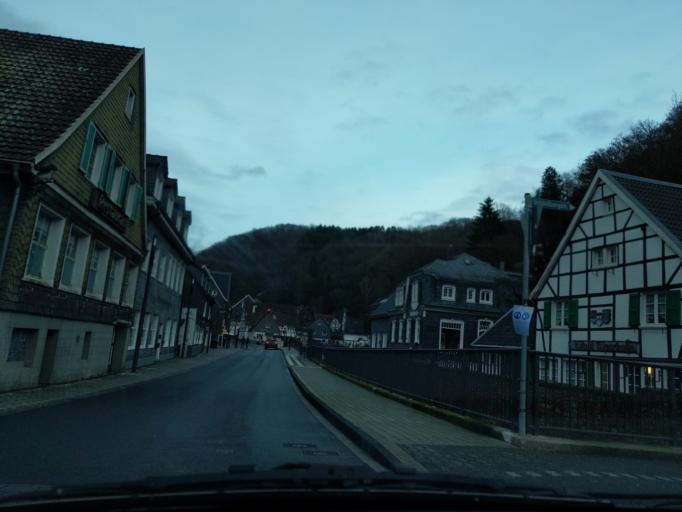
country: DE
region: North Rhine-Westphalia
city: Burscheid
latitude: 51.1380
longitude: 7.1479
